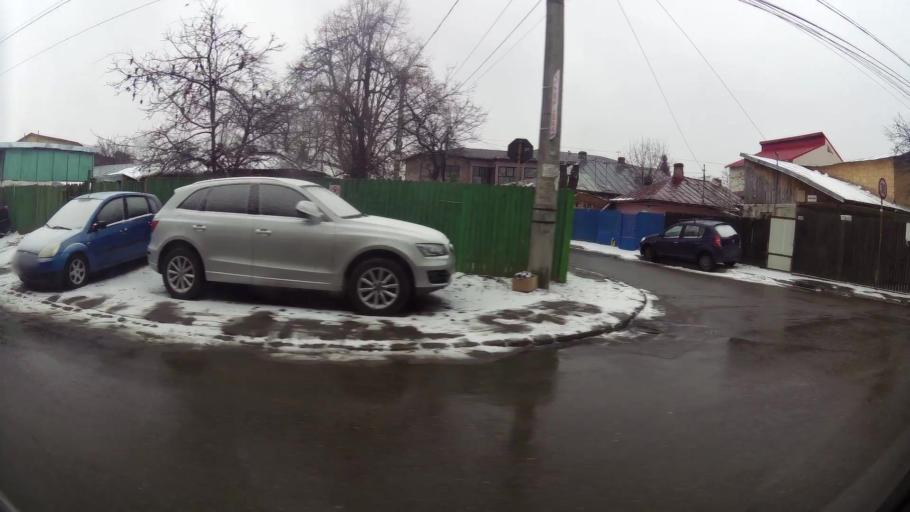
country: RO
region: Prahova
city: Ploiesti
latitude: 44.9461
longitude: 25.9992
